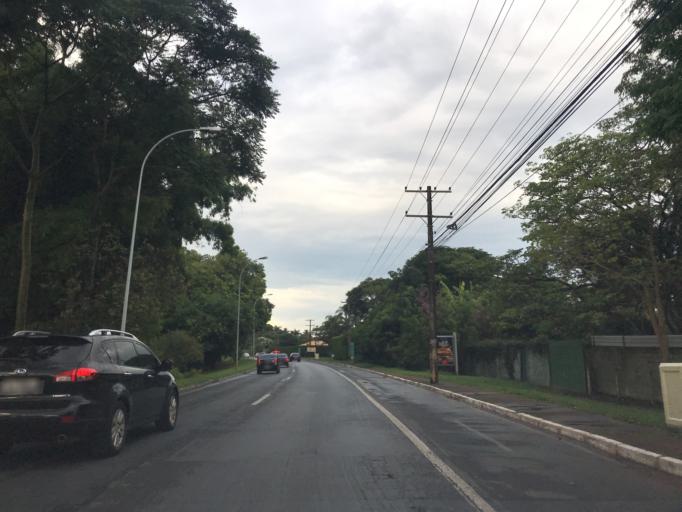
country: BR
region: Federal District
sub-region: Brasilia
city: Brasilia
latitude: -15.8544
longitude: -47.8575
